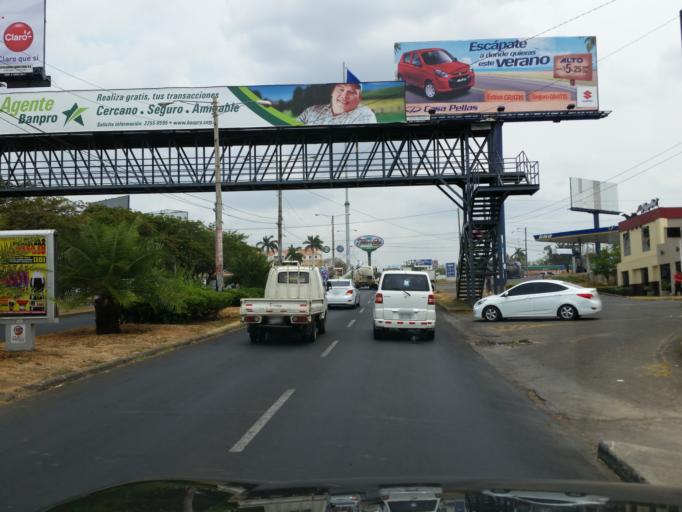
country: NI
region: Managua
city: Managua
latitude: 12.1306
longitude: -86.2669
